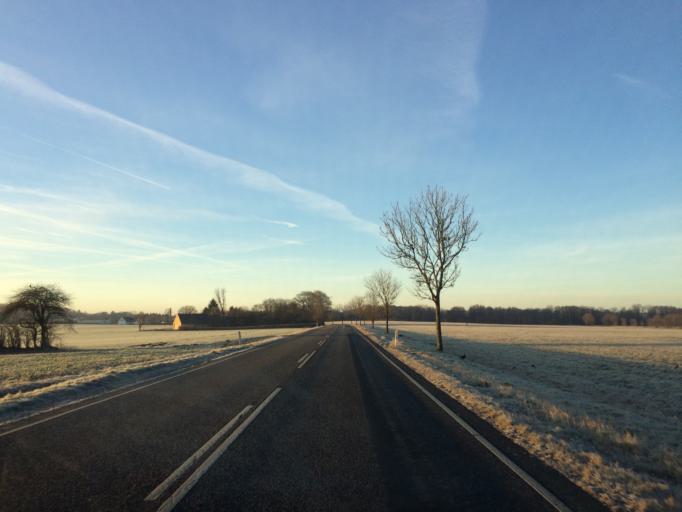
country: DK
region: South Denmark
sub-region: Odense Kommune
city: Bellinge
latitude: 55.2990
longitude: 10.2912
